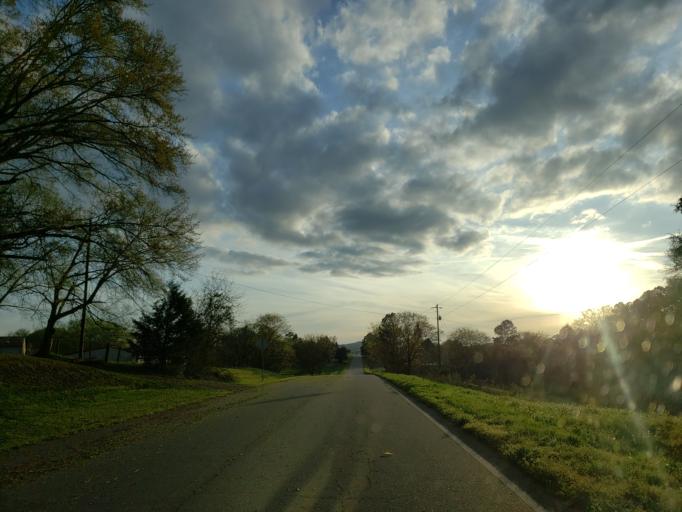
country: US
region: Georgia
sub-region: Bartow County
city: Euharlee
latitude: 34.0924
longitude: -84.9624
